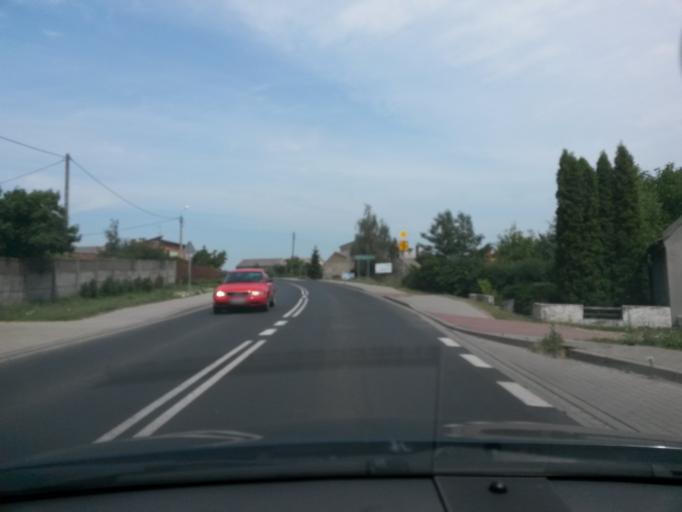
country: PL
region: Greater Poland Voivodeship
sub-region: Powiat sremski
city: Dolsk
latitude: 51.9629
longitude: 17.0783
